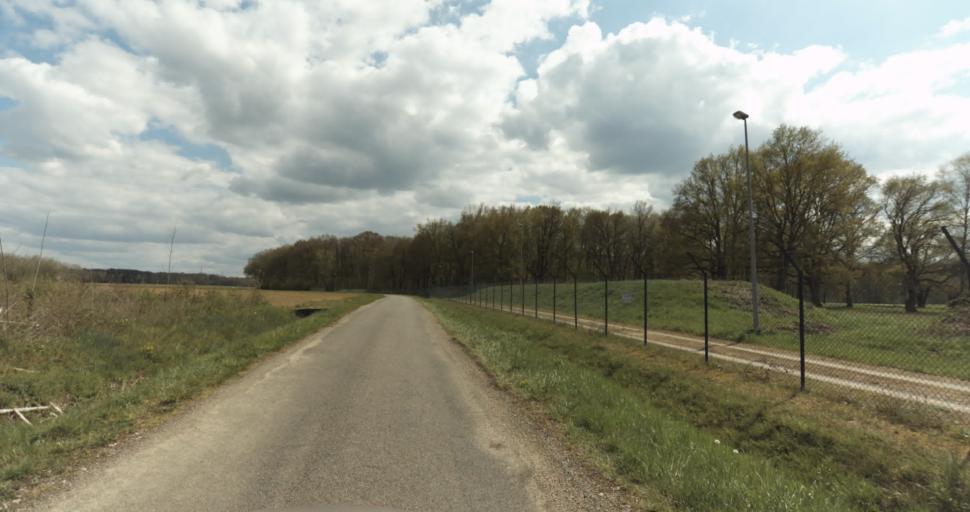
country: FR
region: Bourgogne
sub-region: Departement de la Cote-d'Or
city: Auxonne
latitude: 47.1765
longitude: 5.4103
